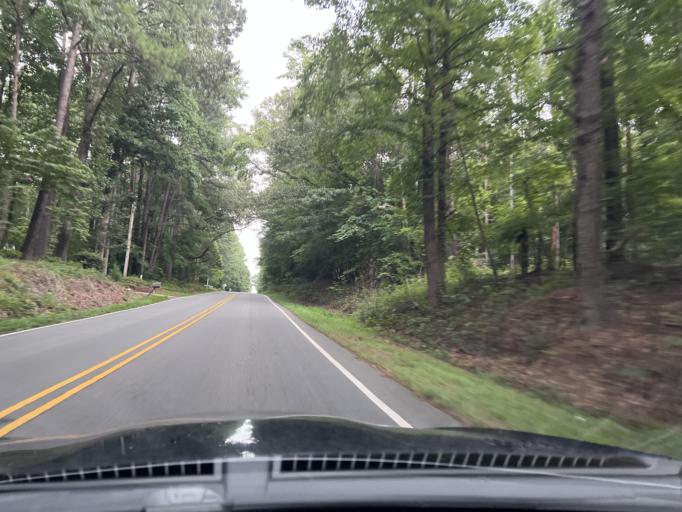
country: US
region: North Carolina
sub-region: Wake County
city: Wake Forest
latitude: 36.0068
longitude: -78.5270
